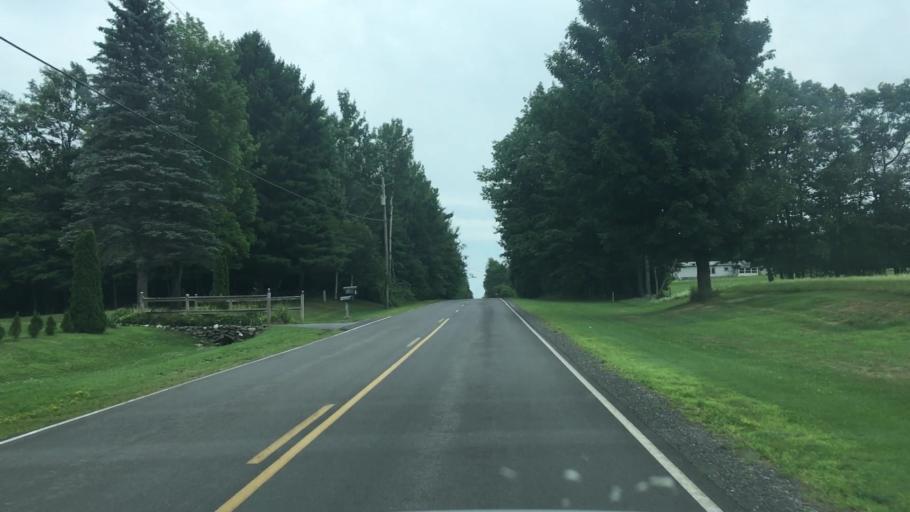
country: US
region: New York
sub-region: Clinton County
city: Peru
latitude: 44.6068
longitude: -73.6295
